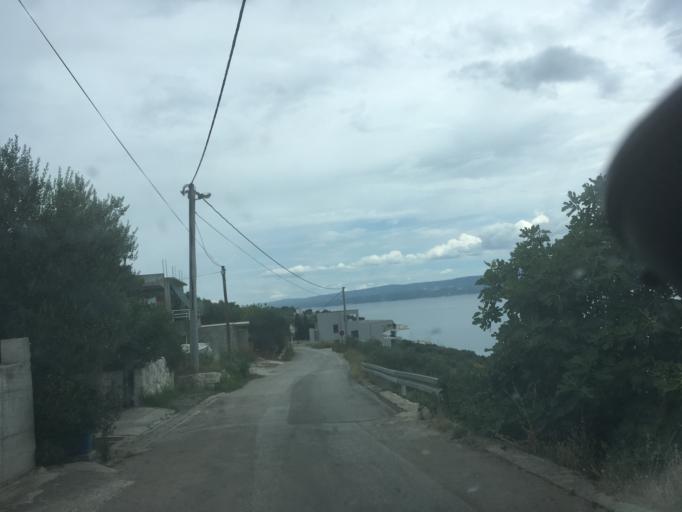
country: HR
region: Splitsko-Dalmatinska
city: Jesenice
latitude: 43.4565
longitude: 16.6213
